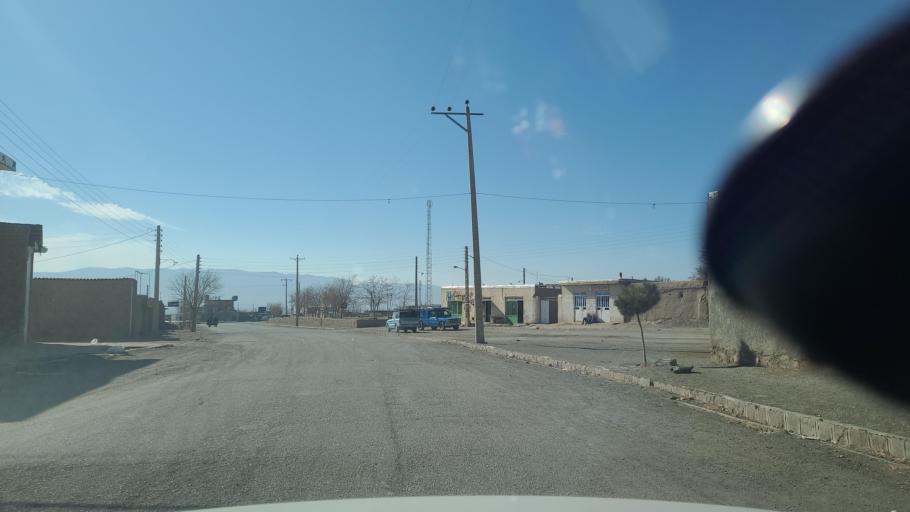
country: IR
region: Razavi Khorasan
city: Dowlatabad
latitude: 35.6224
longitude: 59.4792
